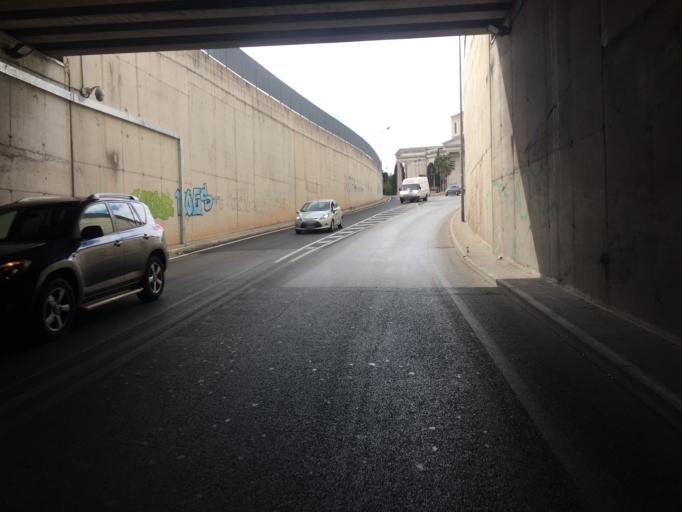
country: IT
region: Apulia
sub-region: Provincia di Bari
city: Bari
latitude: 41.1039
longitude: 16.8499
